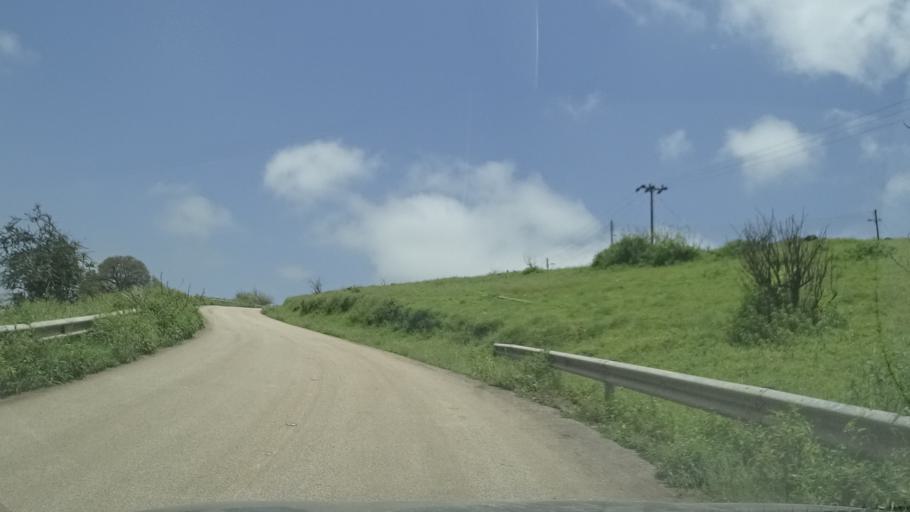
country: OM
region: Zufar
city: Salalah
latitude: 17.2197
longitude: 54.2029
